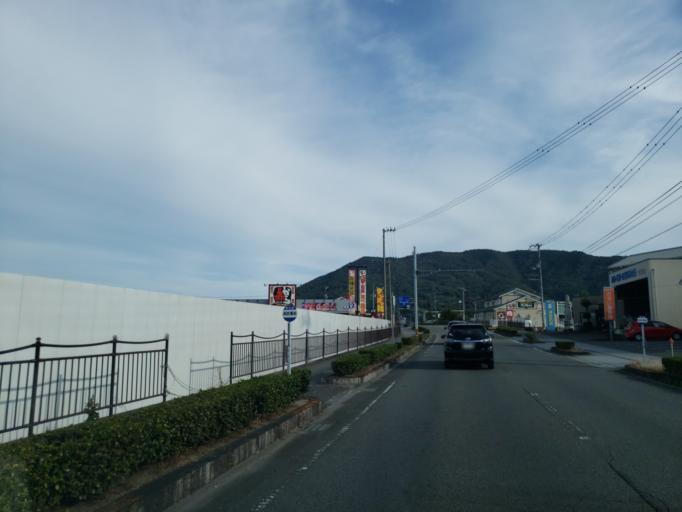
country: JP
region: Tokushima
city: Wakimachi
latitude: 34.0631
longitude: 134.1672
